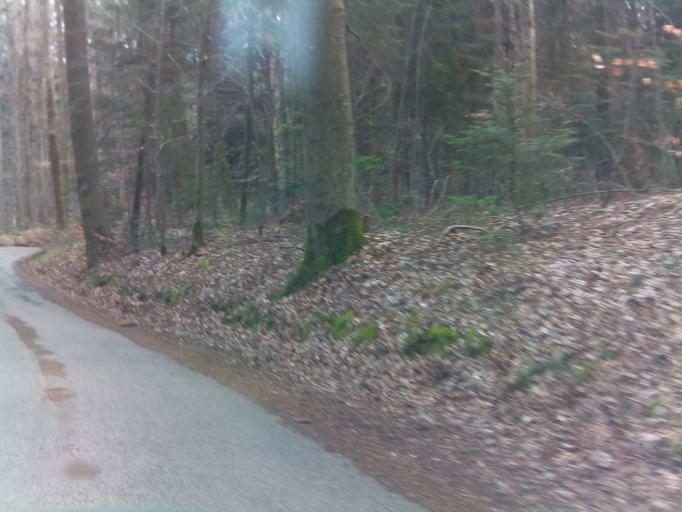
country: DE
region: Baden-Wuerttemberg
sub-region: Regierungsbezirk Stuttgart
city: Lorch
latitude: 48.8280
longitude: 9.6606
